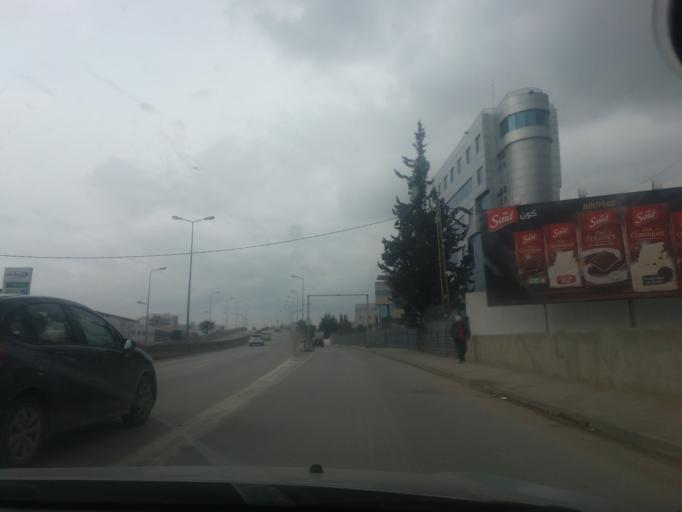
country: TN
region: Tunis
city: Tunis
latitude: 36.8270
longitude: 10.1937
